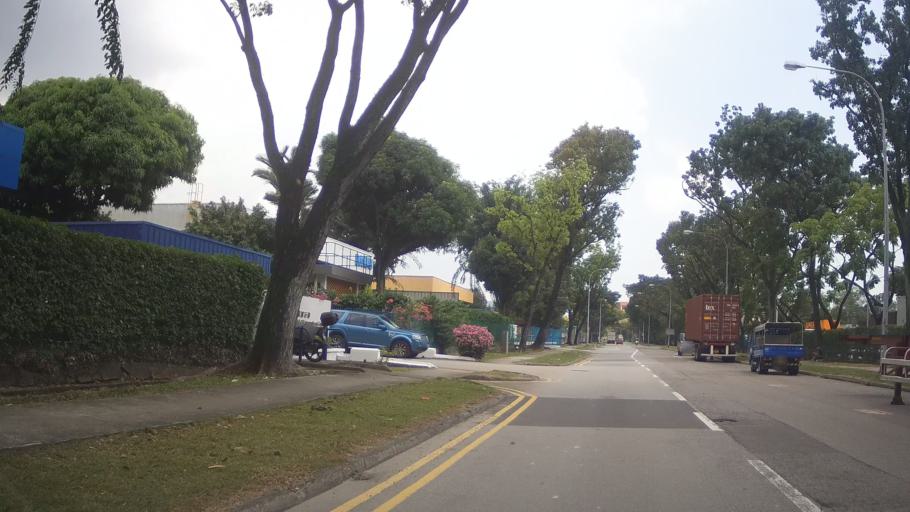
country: MY
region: Johor
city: Johor Bahru
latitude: 1.3124
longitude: 103.6606
